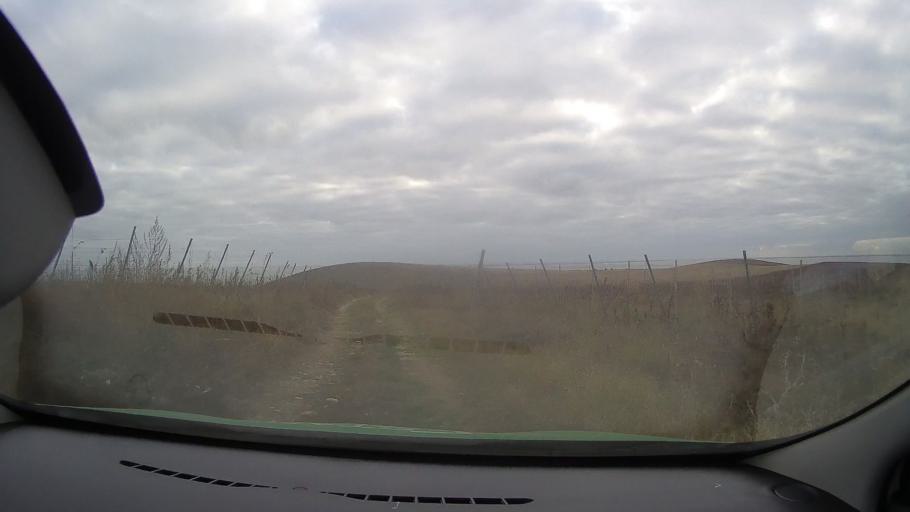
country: RO
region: Tulcea
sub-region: Comuna Jurilovca
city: Jurilovca
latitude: 44.7679
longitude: 28.9178
